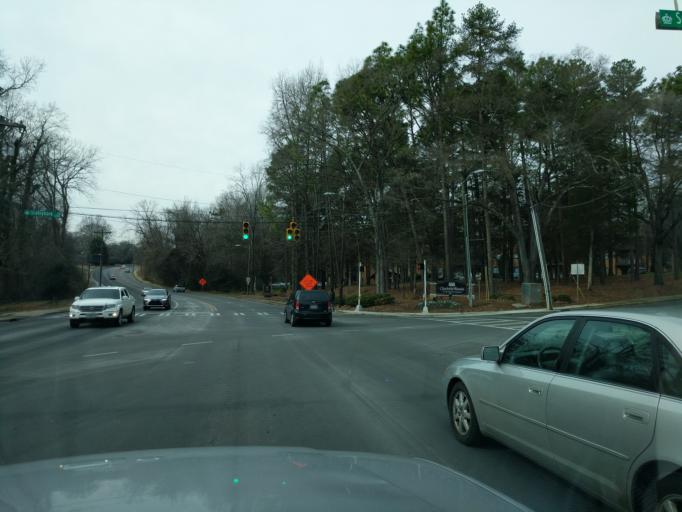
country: US
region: North Carolina
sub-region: Mecklenburg County
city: Charlotte
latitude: 35.1726
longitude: -80.8583
